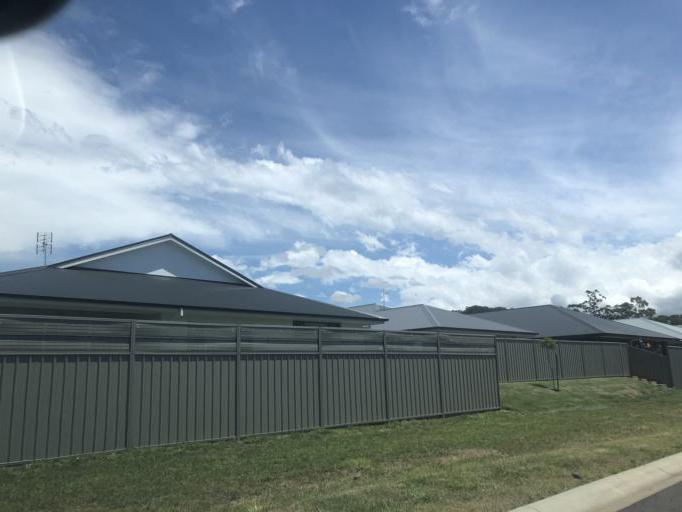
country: AU
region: New South Wales
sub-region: Coffs Harbour
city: Coffs Harbour
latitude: -30.2873
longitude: 153.0938
